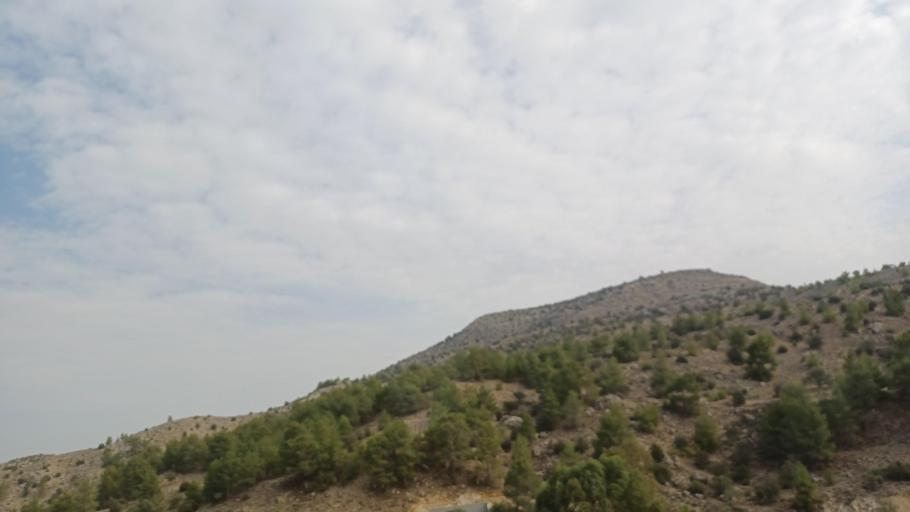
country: CY
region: Lefkosia
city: Klirou
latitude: 35.0511
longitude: 33.1254
